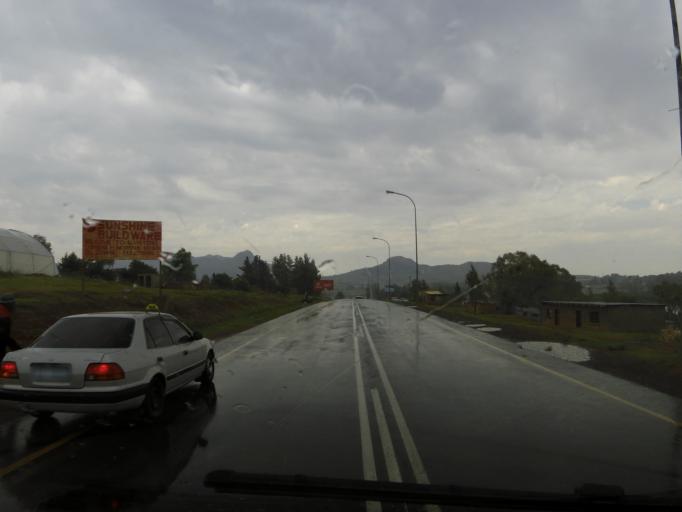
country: LS
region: Mafeteng
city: Mafeteng
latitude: -29.8071
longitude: 27.2519
